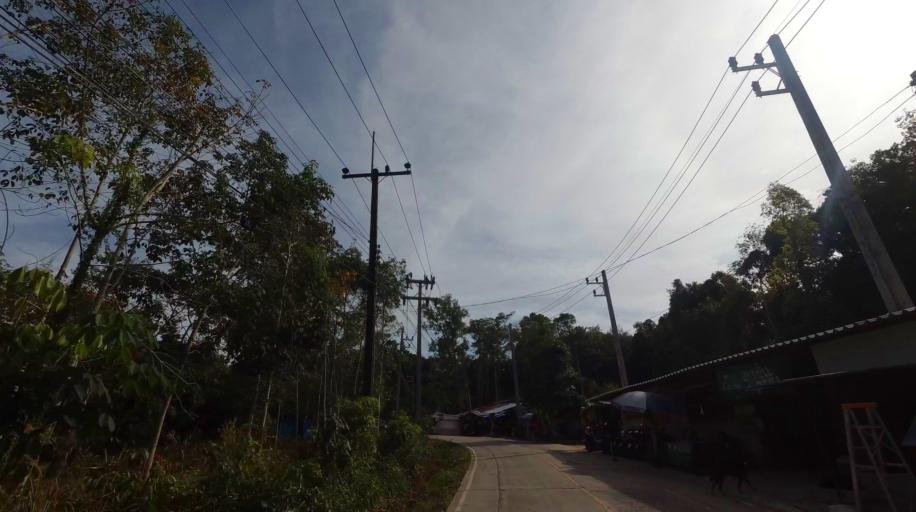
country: TH
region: Trat
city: Ko Kut
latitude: 11.6094
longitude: 102.5419
